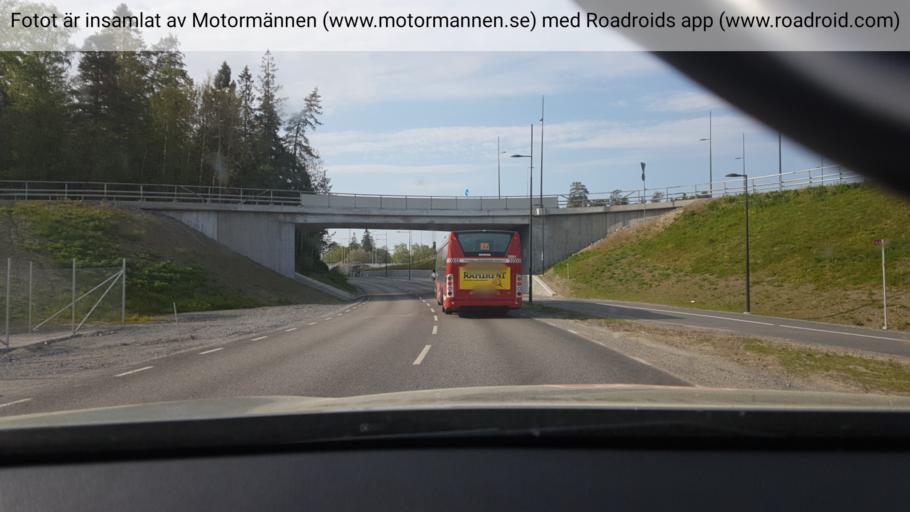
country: SE
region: Stockholm
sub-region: Haninge Kommun
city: Haninge
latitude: 59.1875
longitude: 18.1463
